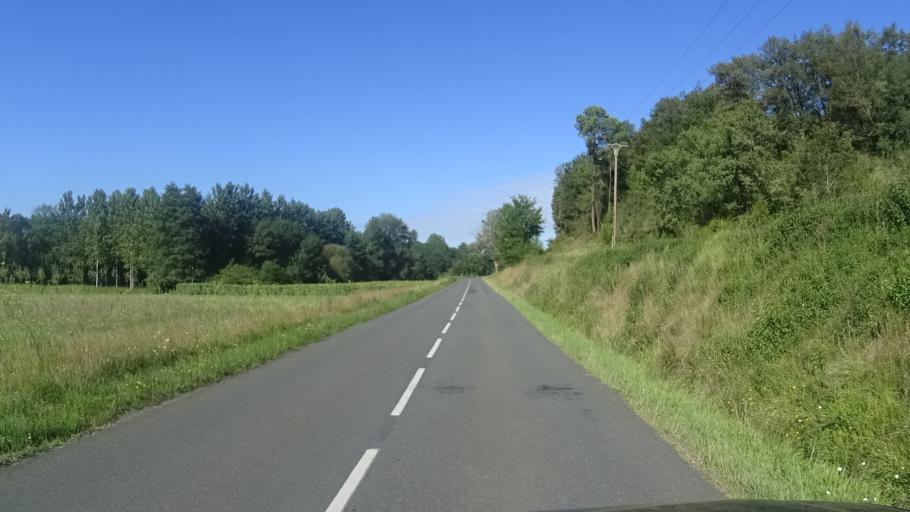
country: FR
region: Aquitaine
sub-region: Departement de la Dordogne
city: Sourzac
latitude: 45.0168
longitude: 0.4341
